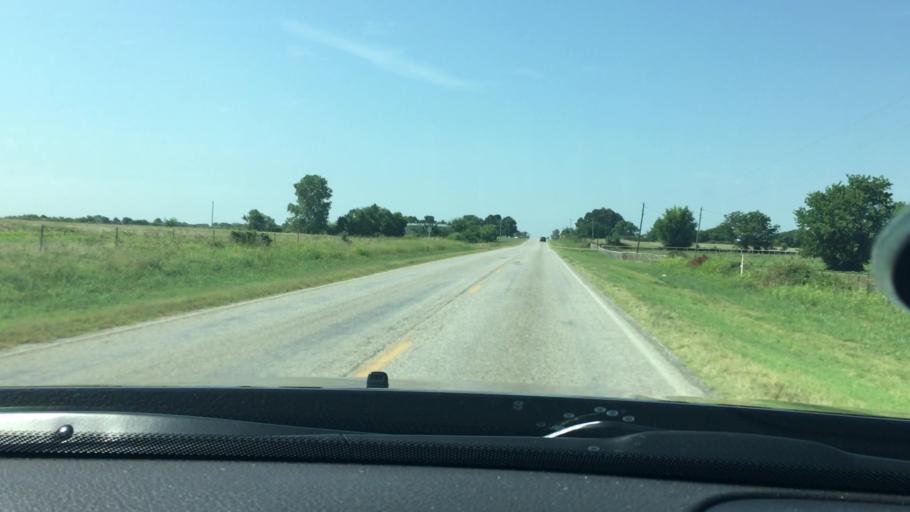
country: US
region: Oklahoma
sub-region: Johnston County
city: Tishomingo
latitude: 34.2830
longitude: -96.4248
